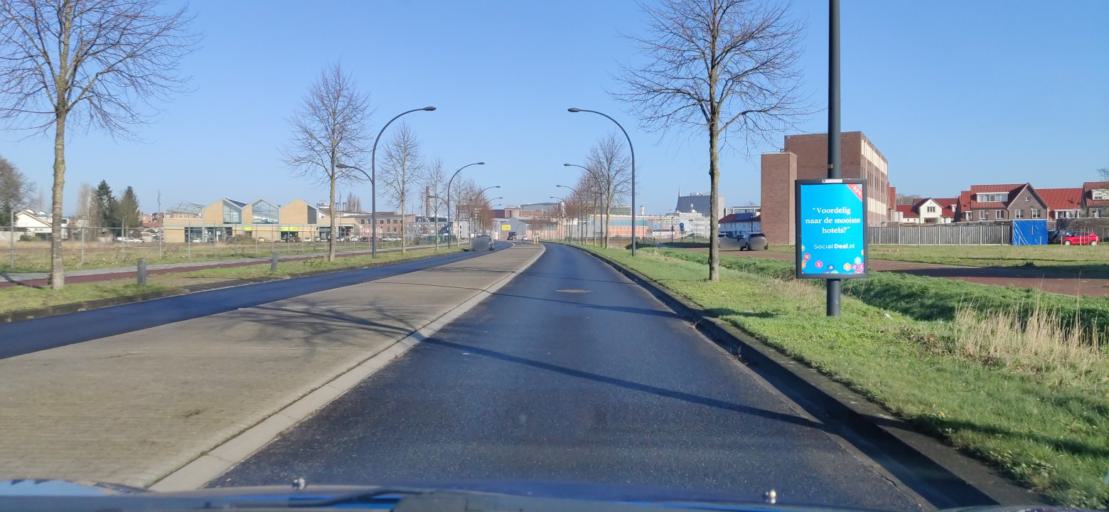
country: NL
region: Overijssel
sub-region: Gemeente Hengelo
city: Hengelo
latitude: 52.2535
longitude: 6.7905
